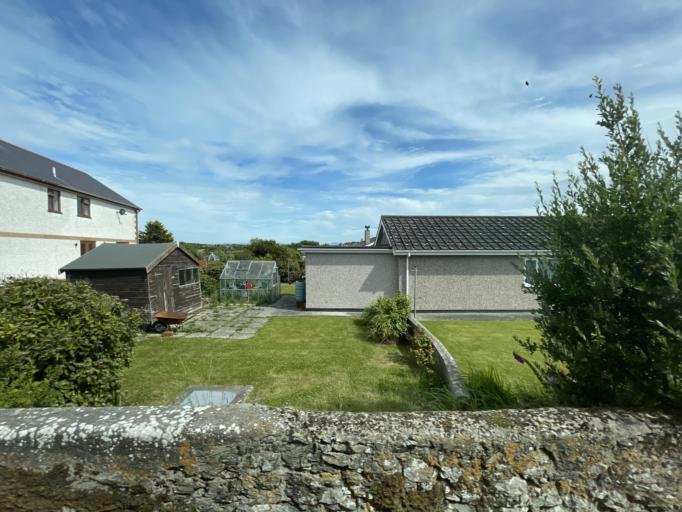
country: GB
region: Wales
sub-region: Anglesey
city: Valley
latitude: 53.2758
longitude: -4.5785
